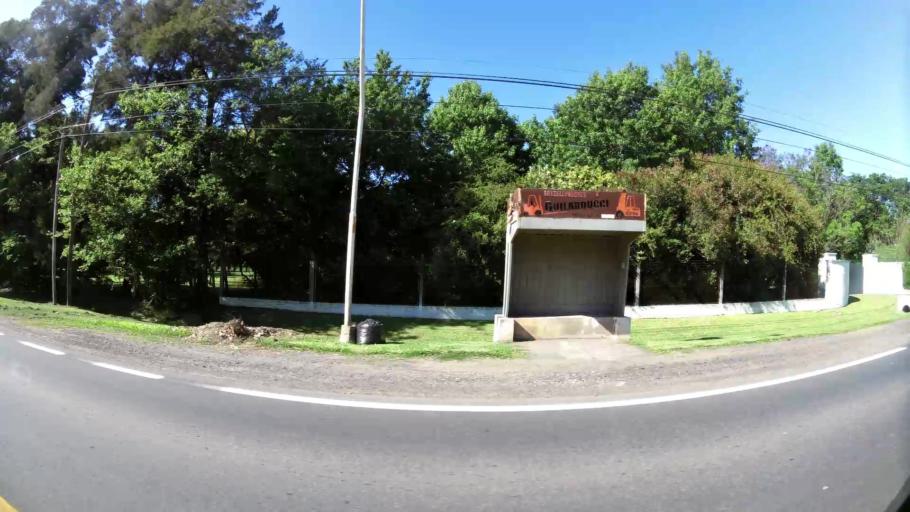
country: AR
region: Santa Fe
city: Esperanza
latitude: -31.4517
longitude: -60.8927
